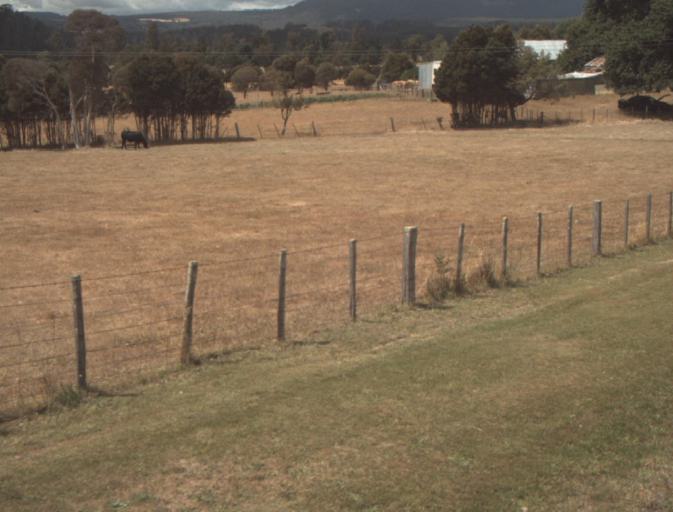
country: AU
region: Tasmania
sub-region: Launceston
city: Mayfield
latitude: -41.2356
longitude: 147.1494
